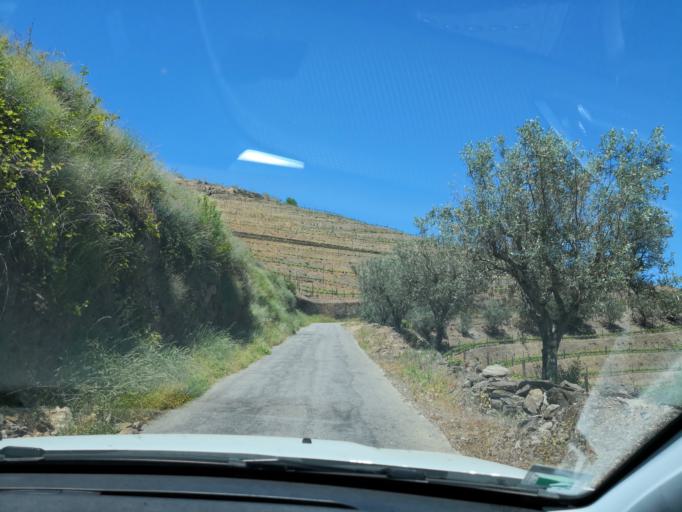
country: PT
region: Vila Real
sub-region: Vila Real
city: Vila Real
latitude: 41.2309
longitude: -7.7206
